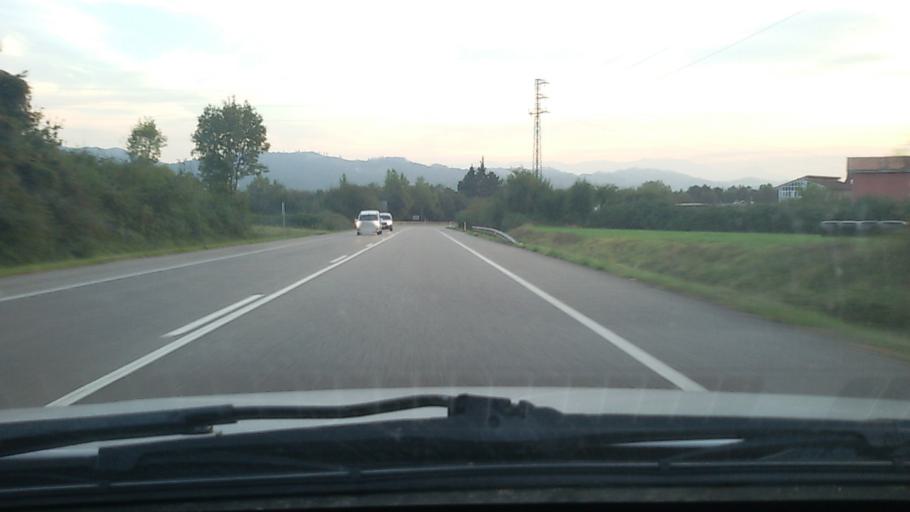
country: ES
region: Asturias
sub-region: Province of Asturias
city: Norena
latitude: 43.3838
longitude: -5.7272
